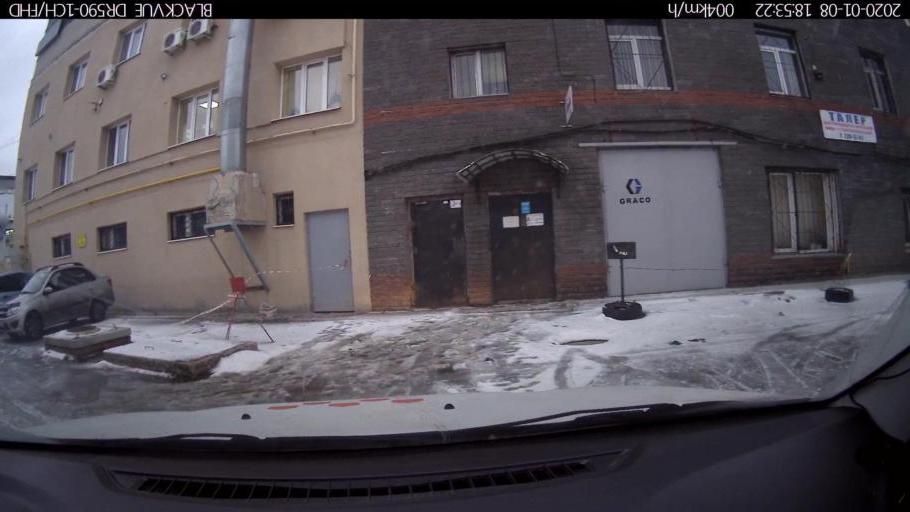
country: RU
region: Nizjnij Novgorod
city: Nizhniy Novgorod
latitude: 56.2712
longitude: 43.9431
